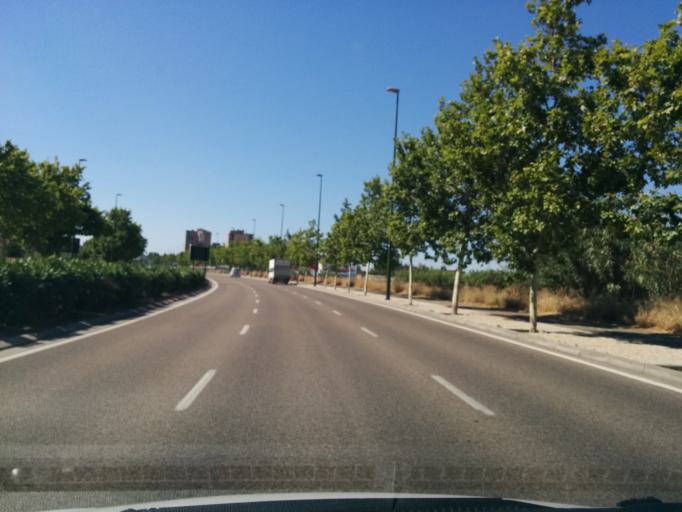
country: ES
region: Aragon
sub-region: Provincia de Zaragoza
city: Zaragoza
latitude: 41.6581
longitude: -0.8531
